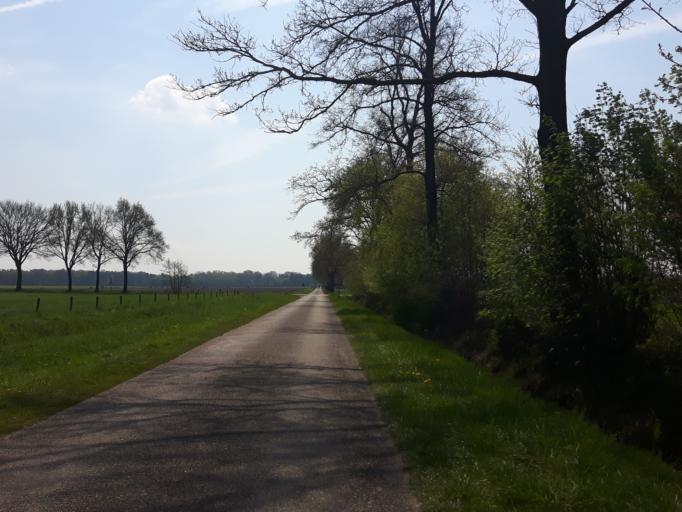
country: DE
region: North Rhine-Westphalia
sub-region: Regierungsbezirk Munster
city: Vreden
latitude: 52.1343
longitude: 6.8400
